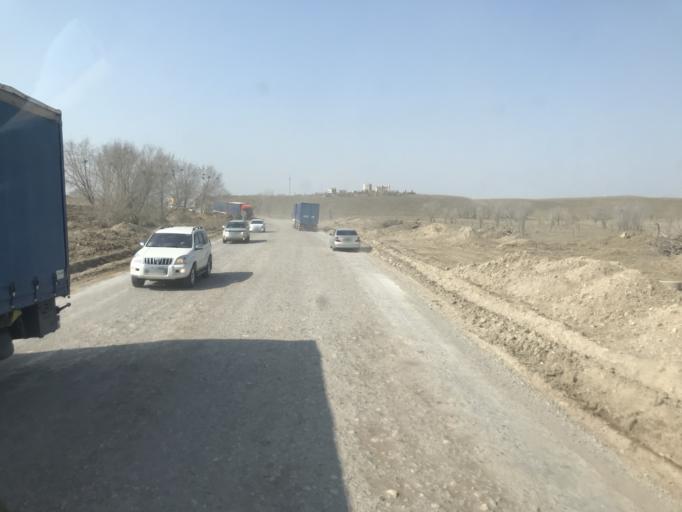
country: KG
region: Chuy
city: Bystrovka
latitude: 43.3209
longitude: 76.0053
